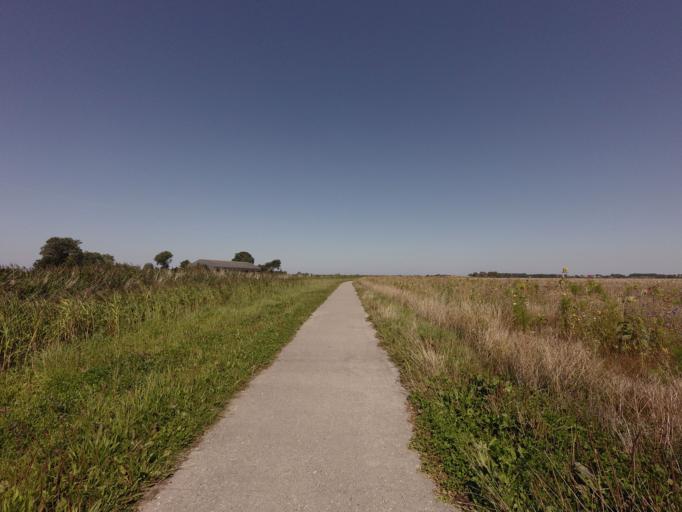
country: NL
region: Friesland
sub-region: Gemeente Dongeradeel
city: Anjum
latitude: 53.3899
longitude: 6.0656
